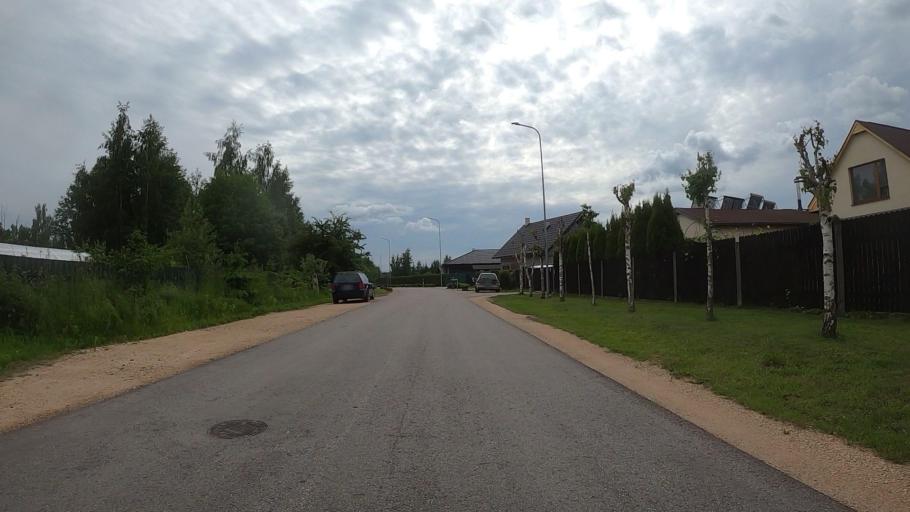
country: LV
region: Olaine
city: Olaine
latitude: 56.7758
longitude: 23.9245
